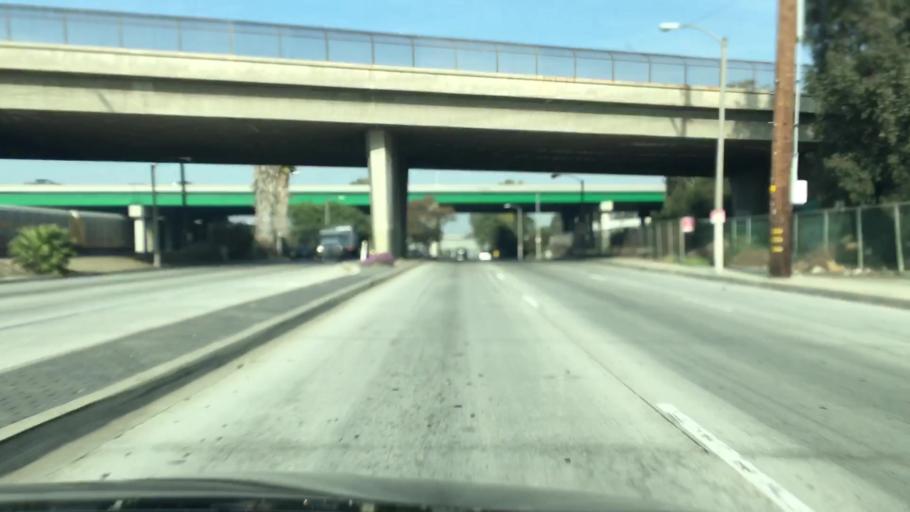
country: US
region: California
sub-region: Los Angeles County
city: Carson
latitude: 33.8241
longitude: -118.2288
